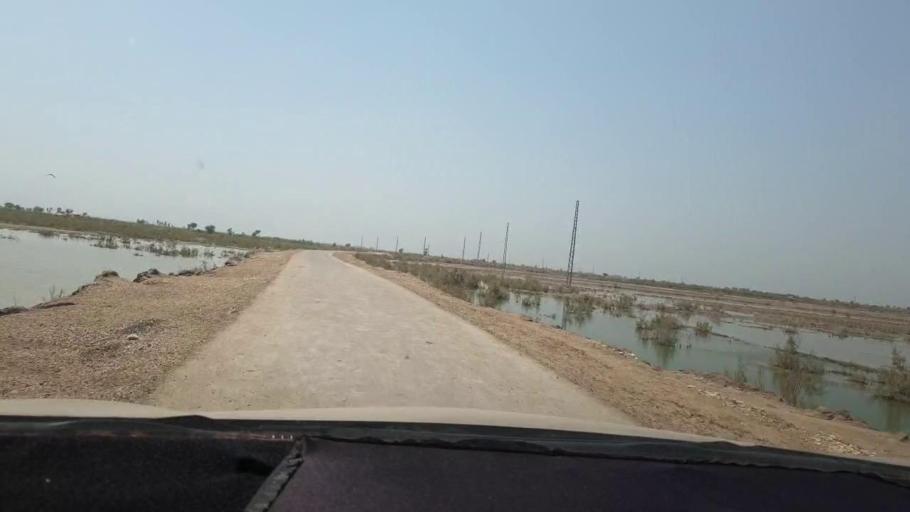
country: PK
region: Sindh
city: Shahdadkot
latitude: 27.8341
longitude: 67.8848
